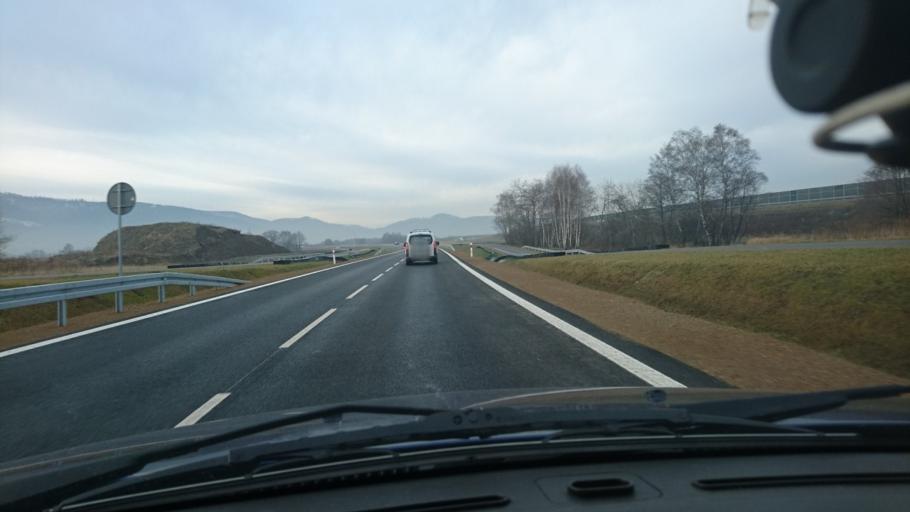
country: PL
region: Silesian Voivodeship
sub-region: Powiat bielski
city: Rybarzowice
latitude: 49.7401
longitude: 19.0985
